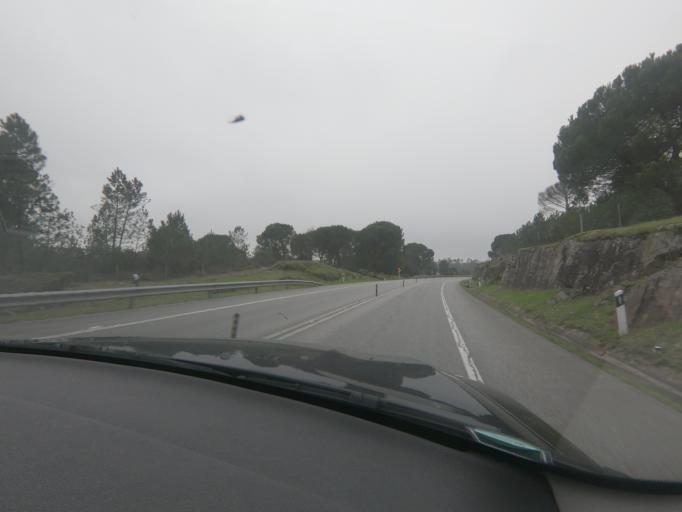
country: PT
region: Viseu
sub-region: Concelho de Tondela
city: Tondela
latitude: 40.5296
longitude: -8.0677
